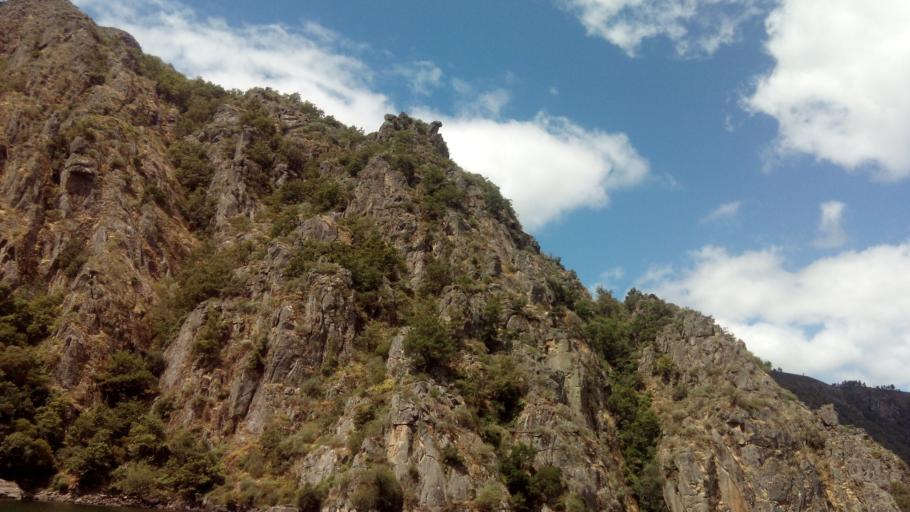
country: ES
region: Galicia
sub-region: Provincia de Lugo
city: Sober
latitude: 42.3893
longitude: -7.6214
